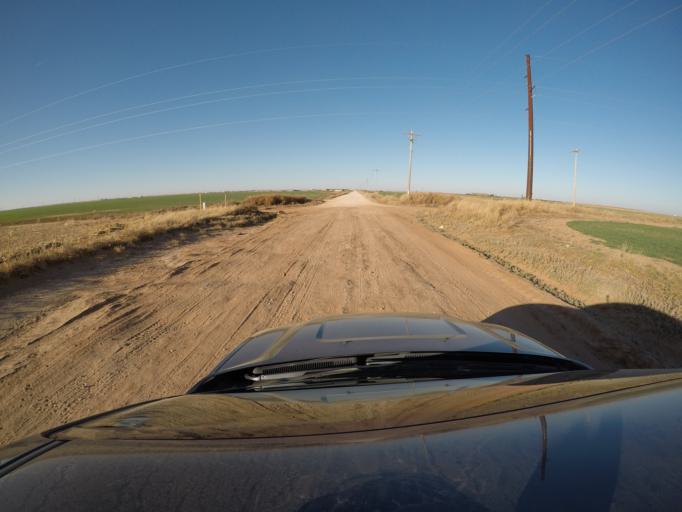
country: US
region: New Mexico
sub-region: Curry County
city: Texico
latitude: 34.3607
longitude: -103.1083
